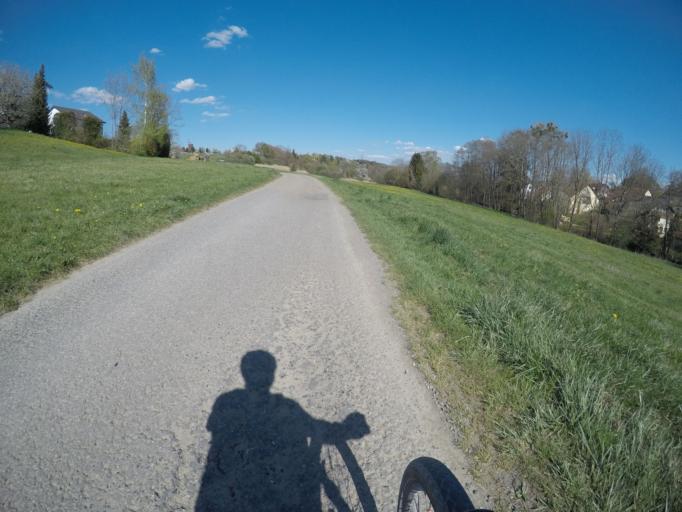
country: DE
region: Baden-Wuerttemberg
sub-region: Regierungsbezirk Stuttgart
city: Weil im Schonbuch
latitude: 48.6262
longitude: 9.0654
